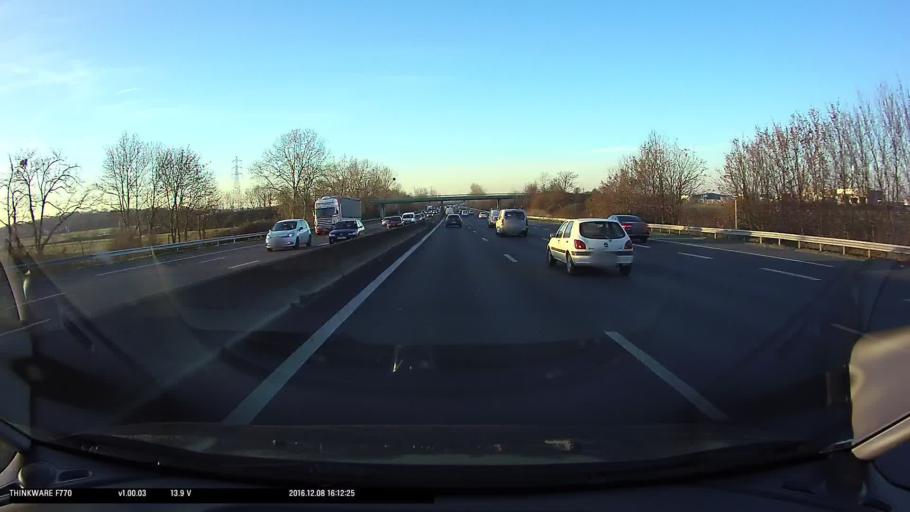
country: FR
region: Ile-de-France
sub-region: Departement du Val-d'Oise
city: Pierrelaye
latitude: 49.0174
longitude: 2.1423
